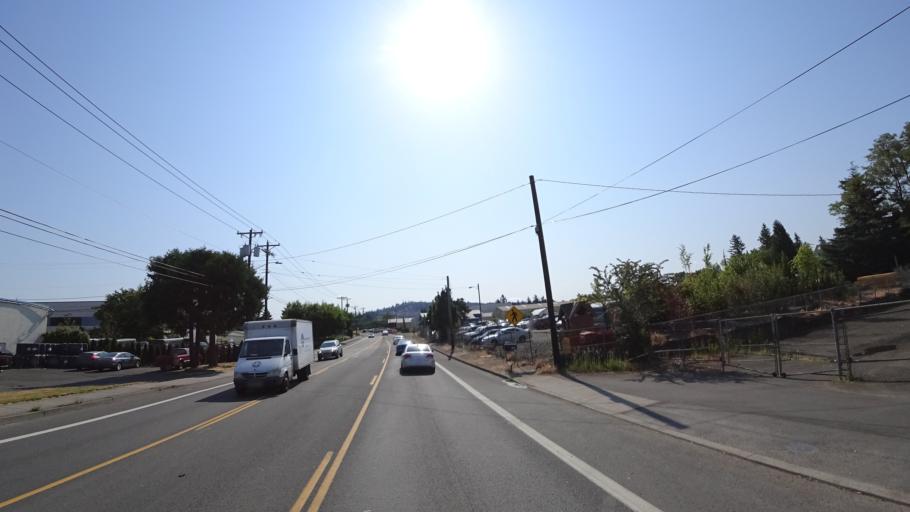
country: US
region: Oregon
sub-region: Multnomah County
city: Lents
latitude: 45.4559
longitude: -122.5896
